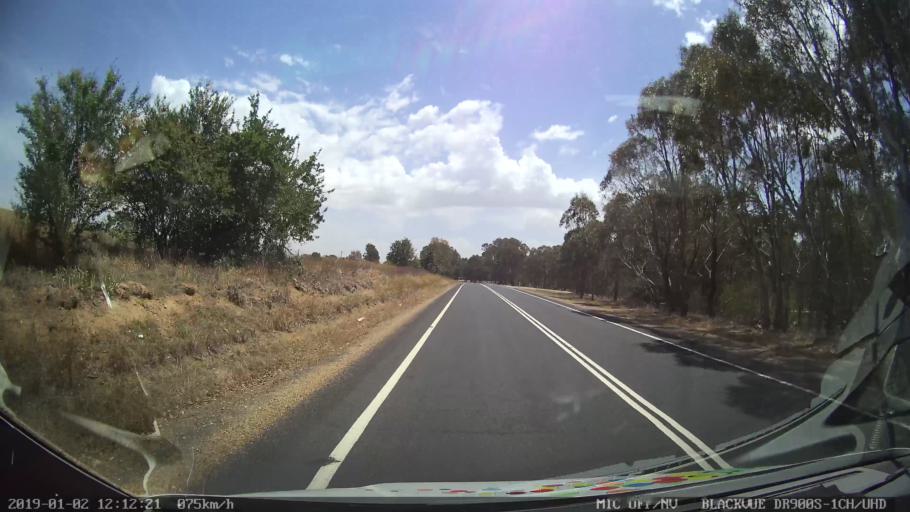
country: AU
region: New South Wales
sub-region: Young
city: Young
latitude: -34.4380
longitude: 148.2549
